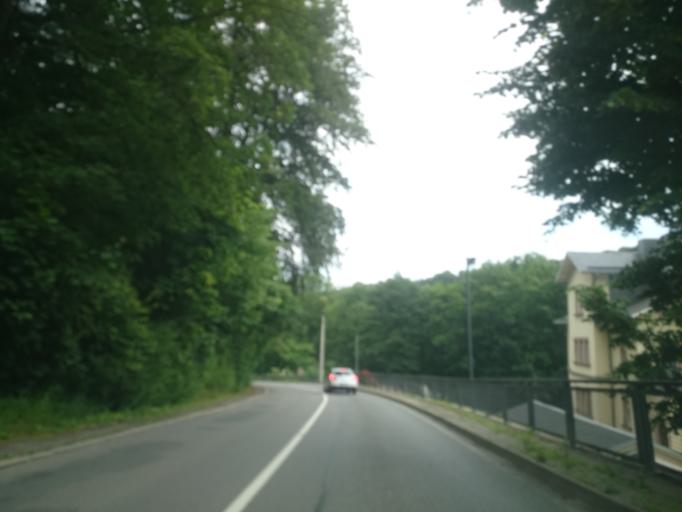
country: DE
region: Saxony
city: Grunhainichen
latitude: 50.7702
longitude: 13.1620
